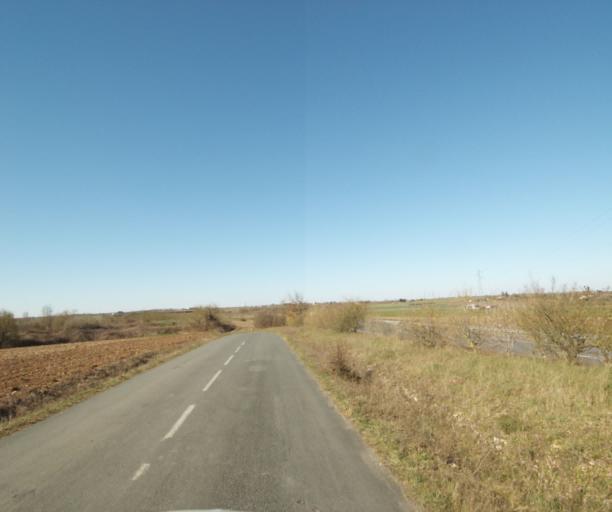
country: FR
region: Poitou-Charentes
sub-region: Departement des Deux-Sevres
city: Bessines
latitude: 46.3364
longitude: -0.5041
